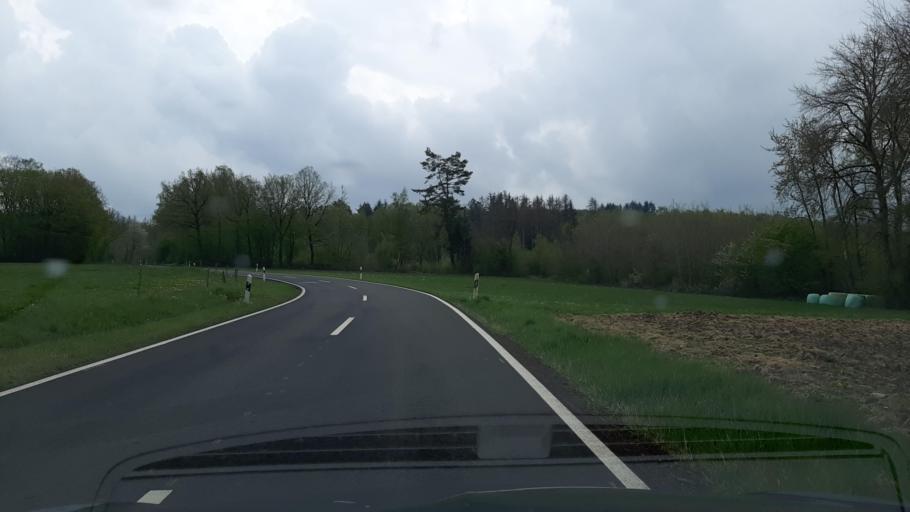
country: DE
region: Rheinland-Pfalz
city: Nortershausen
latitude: 50.2504
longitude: 7.4978
